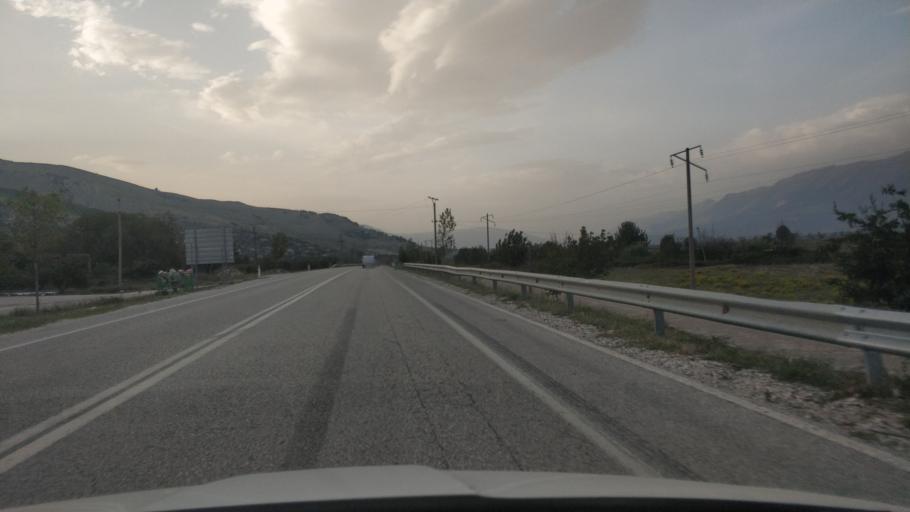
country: AL
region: Gjirokaster
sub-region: Rrethi i Gjirokastres
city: Libohove
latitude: 39.9549
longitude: 20.2510
